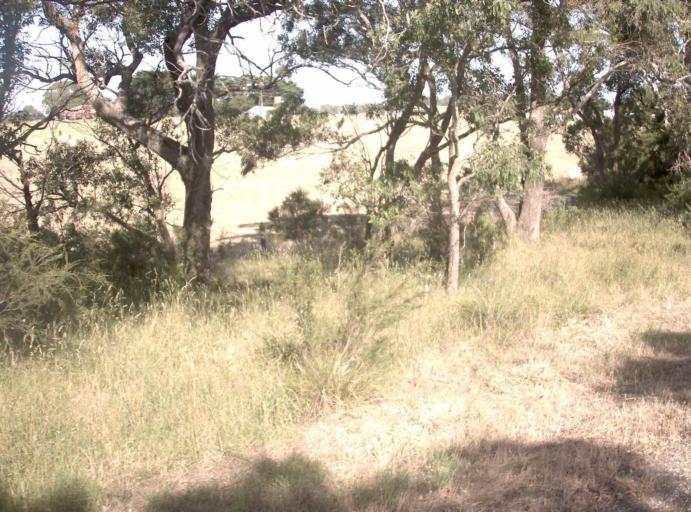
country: AU
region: Victoria
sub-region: East Gippsland
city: Lakes Entrance
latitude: -37.8119
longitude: 147.8464
